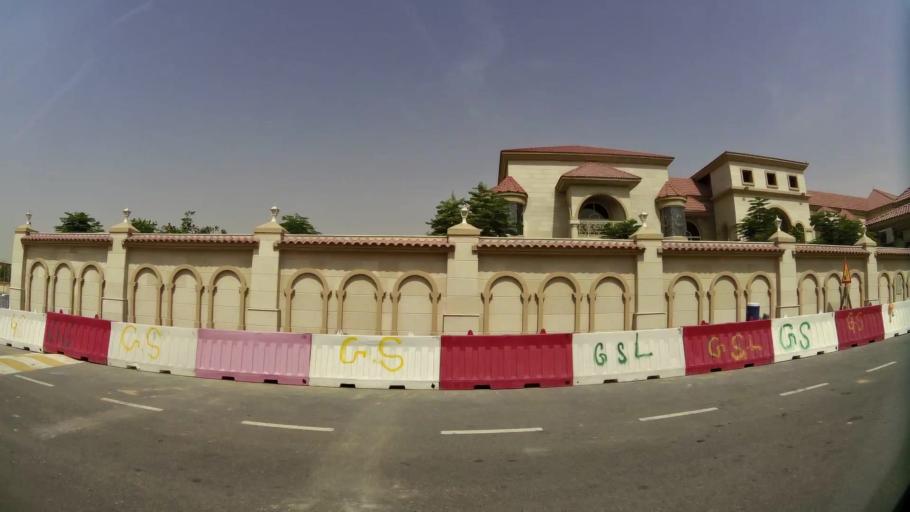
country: AE
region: Ash Shariqah
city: Sharjah
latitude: 25.2442
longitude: 55.4975
